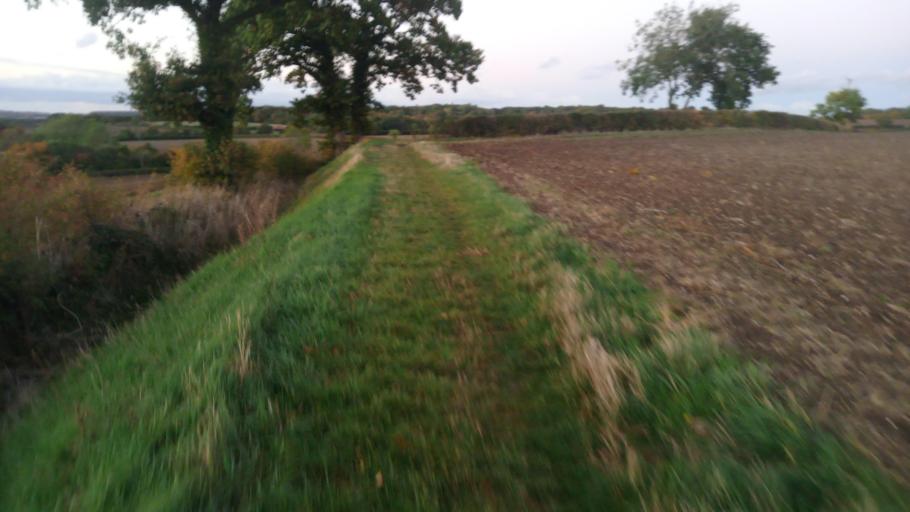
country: GB
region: England
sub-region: Cambridgeshire
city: Linton
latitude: 52.0552
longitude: 0.3176
